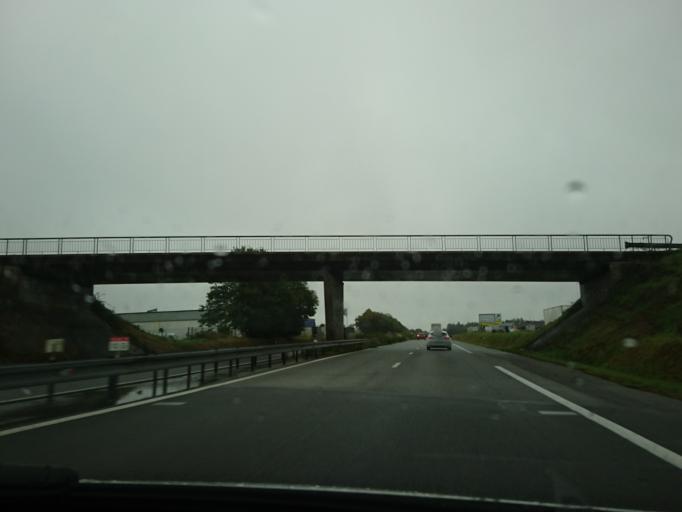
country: FR
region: Brittany
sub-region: Departement du Finistere
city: Mellac
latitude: 47.8702
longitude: -3.5959
